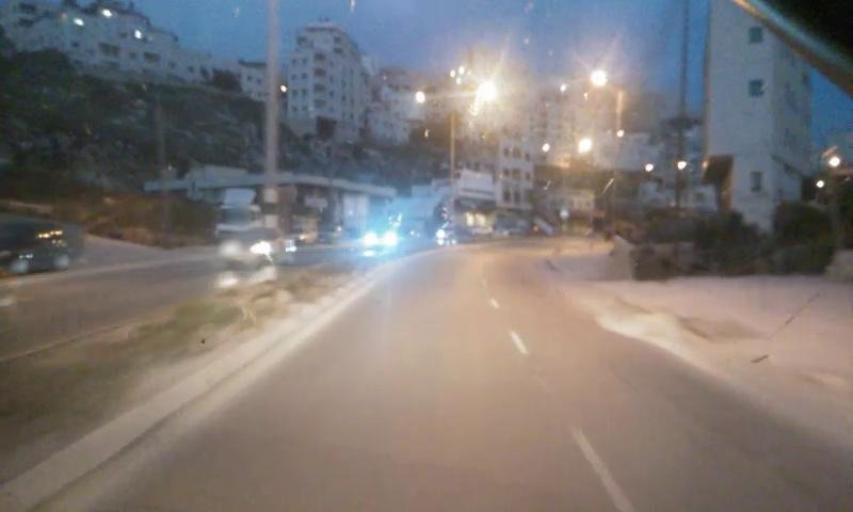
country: PS
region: West Bank
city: Zawata
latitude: 32.2403
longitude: 35.2306
